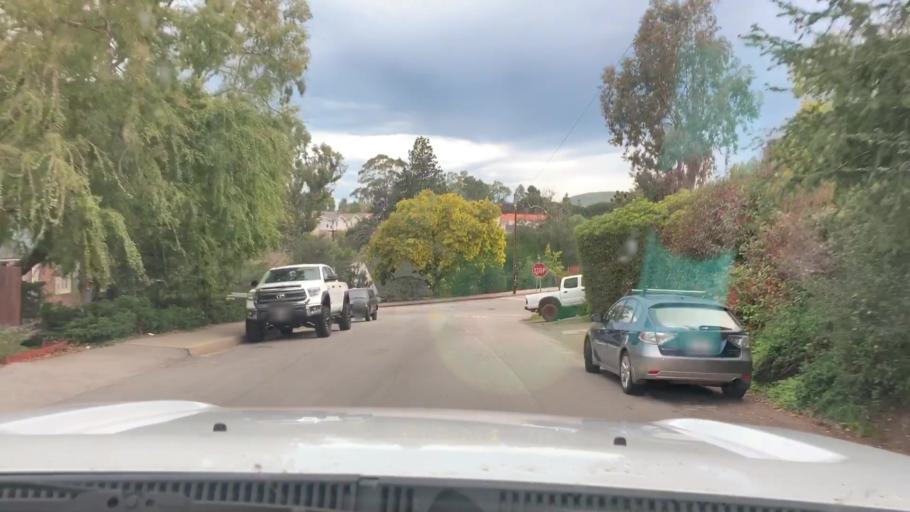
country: US
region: California
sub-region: San Luis Obispo County
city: San Luis Obispo
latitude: 35.2958
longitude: -120.6597
